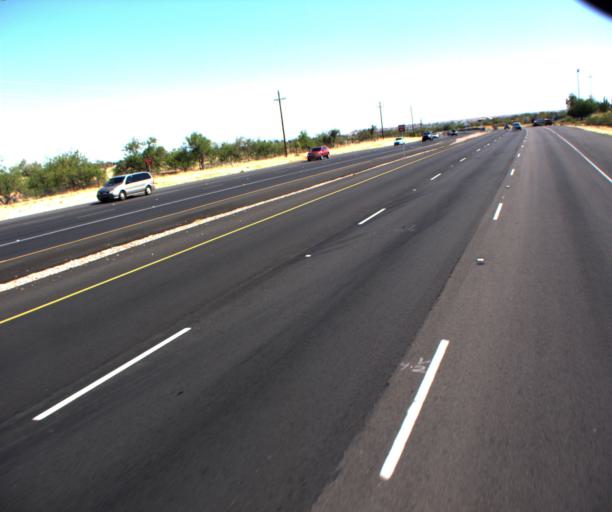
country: US
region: Arizona
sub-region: Pima County
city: Catalina
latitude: 32.4750
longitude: -110.9227
